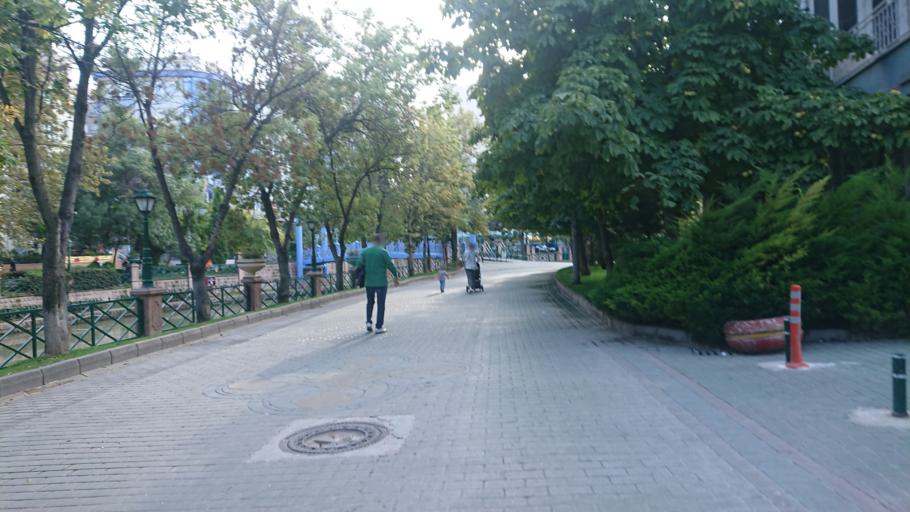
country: TR
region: Eskisehir
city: Eskisehir
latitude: 39.7769
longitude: 30.5115
